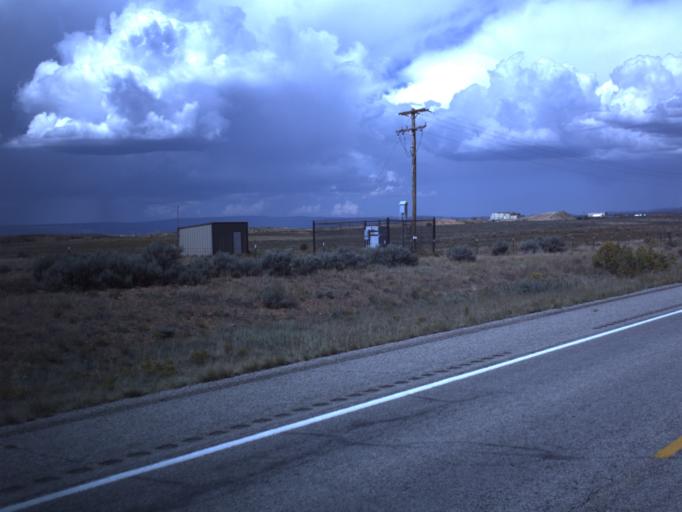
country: US
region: Utah
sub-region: San Juan County
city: Blanding
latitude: 37.5223
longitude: -109.4941
